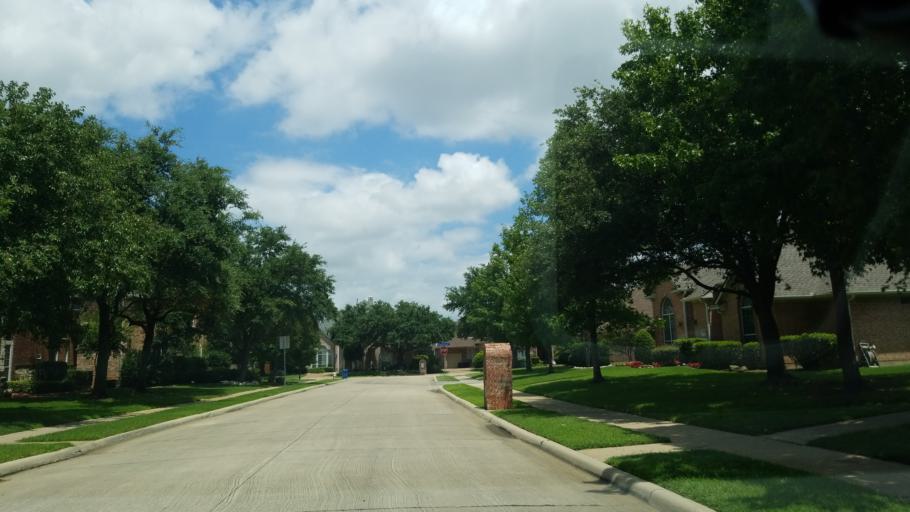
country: US
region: Texas
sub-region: Dallas County
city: Carrollton
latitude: 32.9596
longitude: -96.9508
